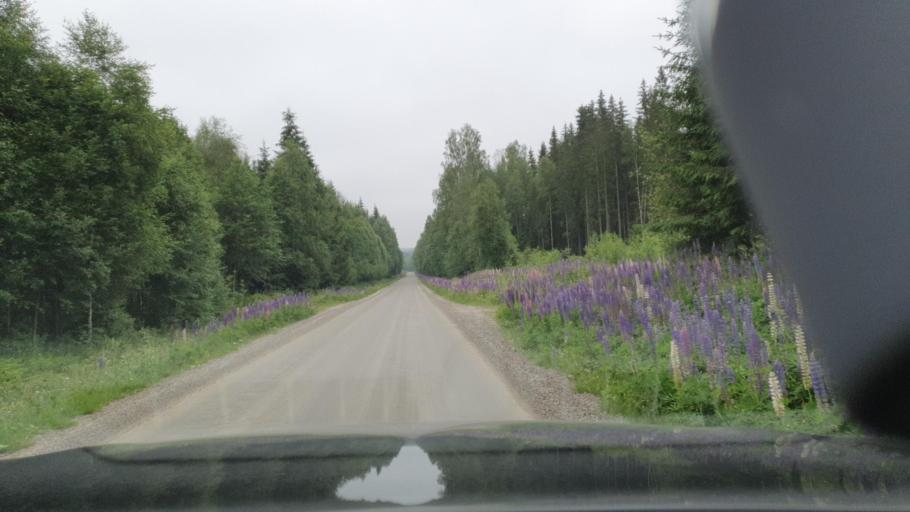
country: SE
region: Vaermland
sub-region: Arvika Kommun
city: Arvika
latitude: 59.8041
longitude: 12.7486
